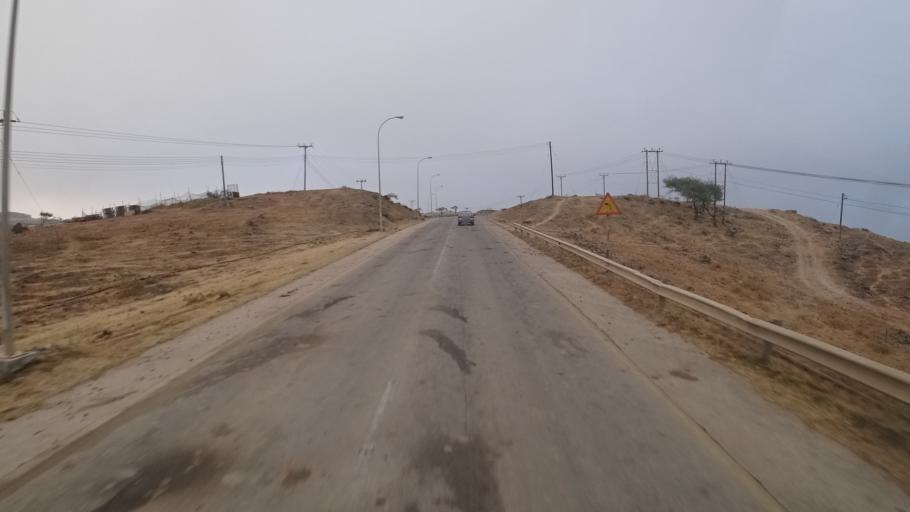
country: OM
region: Zufar
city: Salalah
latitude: 17.1283
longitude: 53.9766
